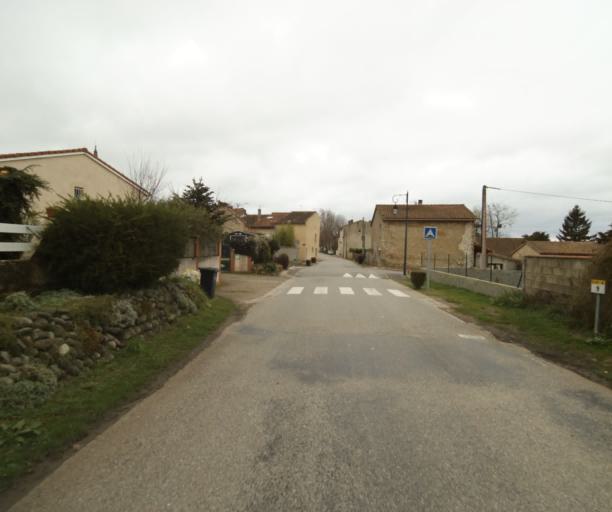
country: FR
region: Midi-Pyrenees
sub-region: Departement de l'Ariege
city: Pamiers
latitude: 43.1555
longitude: 1.6359
